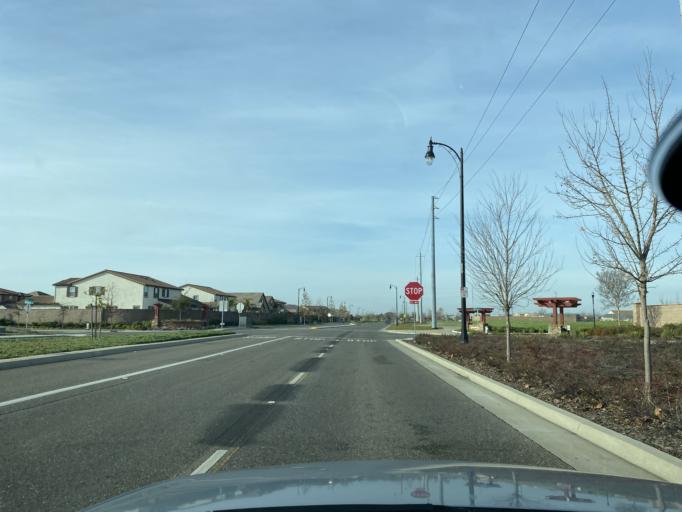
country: US
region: California
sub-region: Sacramento County
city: Elk Grove
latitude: 38.3946
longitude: -121.3917
